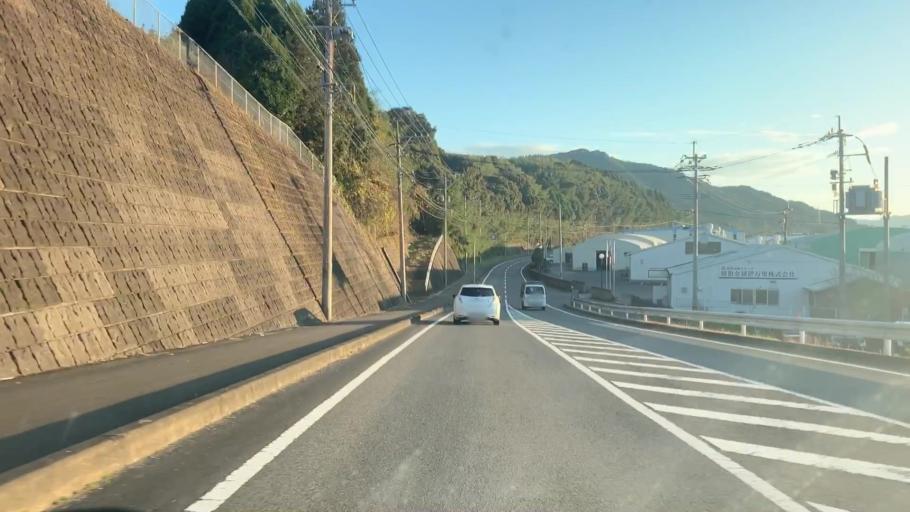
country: JP
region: Saga Prefecture
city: Imaricho-ko
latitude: 33.2905
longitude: 129.9706
